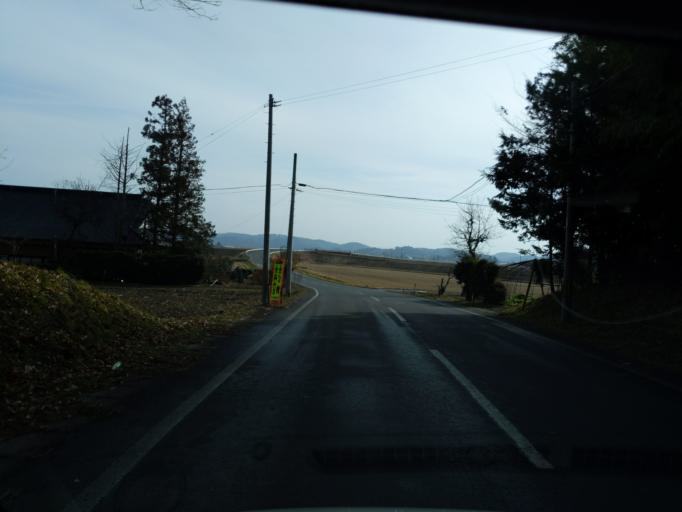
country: JP
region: Iwate
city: Ichinoseki
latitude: 38.7831
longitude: 141.1738
